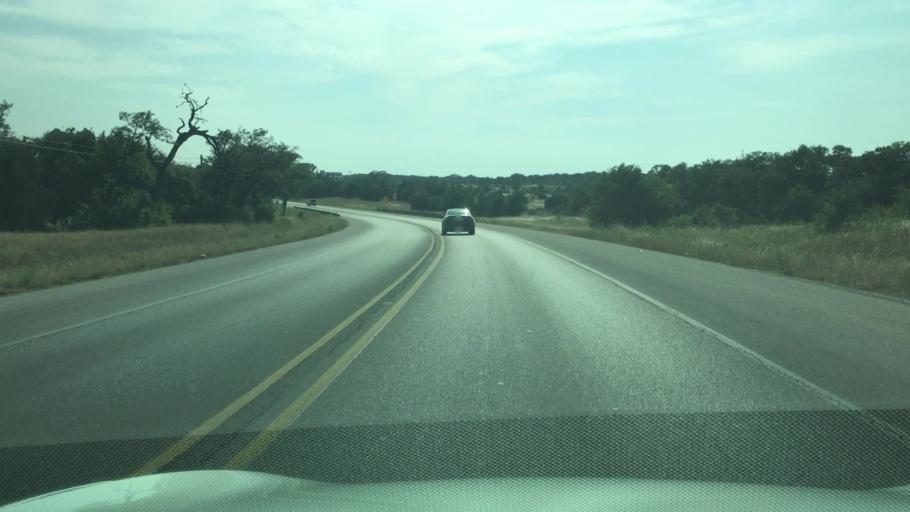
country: US
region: Texas
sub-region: Hays County
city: Wimberley
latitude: 29.9176
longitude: -98.0421
